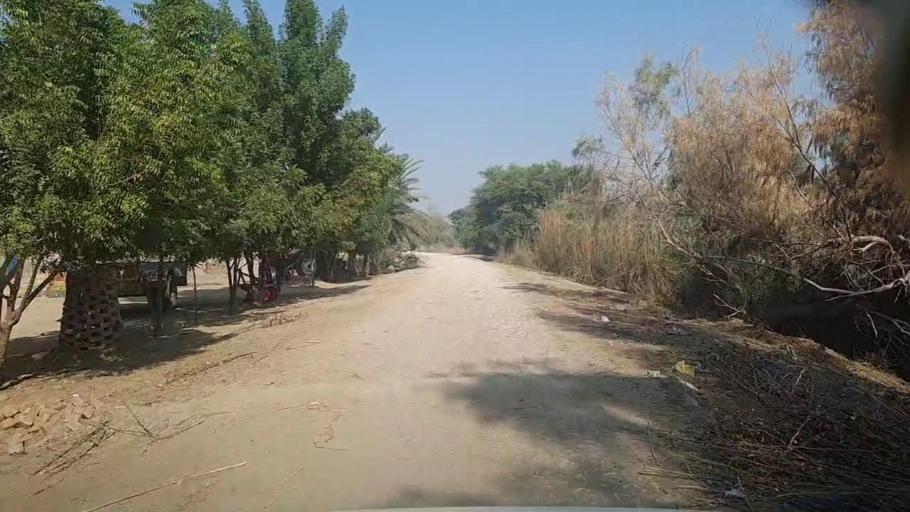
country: PK
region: Sindh
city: Kandiari
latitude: 26.9364
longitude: 68.5303
